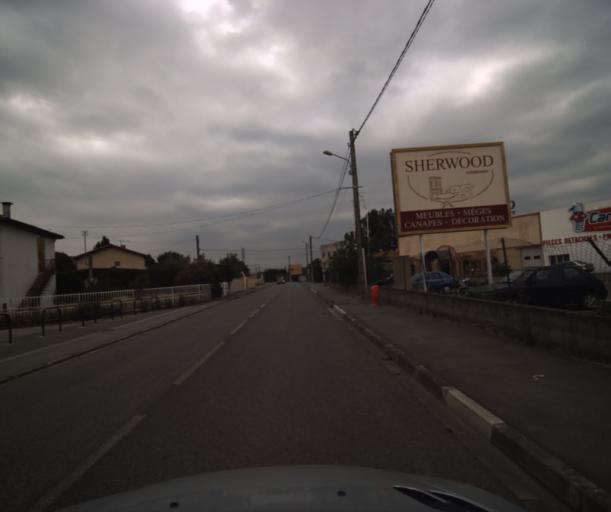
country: FR
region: Midi-Pyrenees
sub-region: Departement de la Haute-Garonne
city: Portet-sur-Garonne
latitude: 43.5384
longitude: 1.4028
